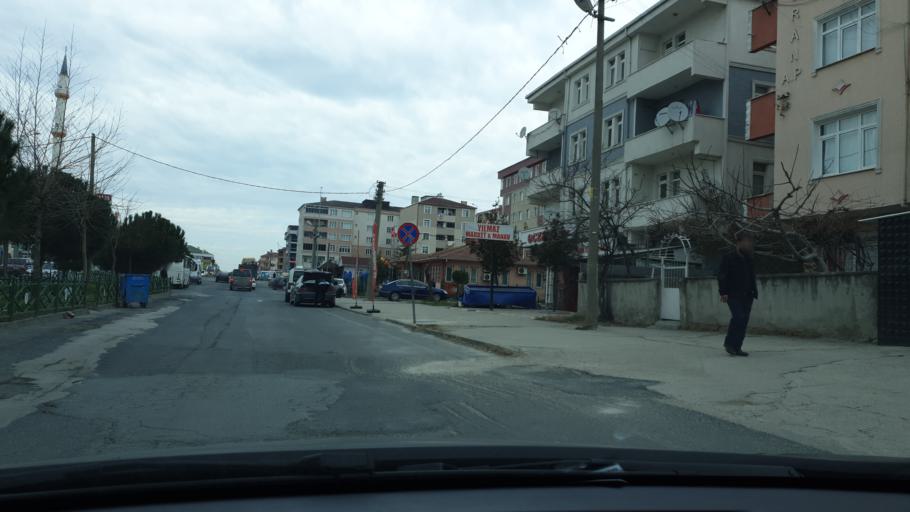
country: TR
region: Tekirdag
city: Cerkezkoey
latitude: 41.2843
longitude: 27.9884
